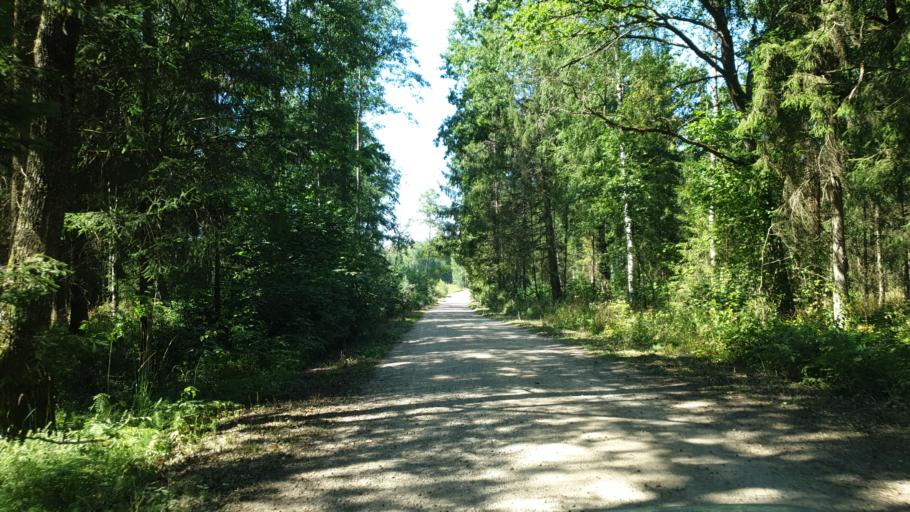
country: LT
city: Sirvintos
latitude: 54.8997
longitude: 24.8969
